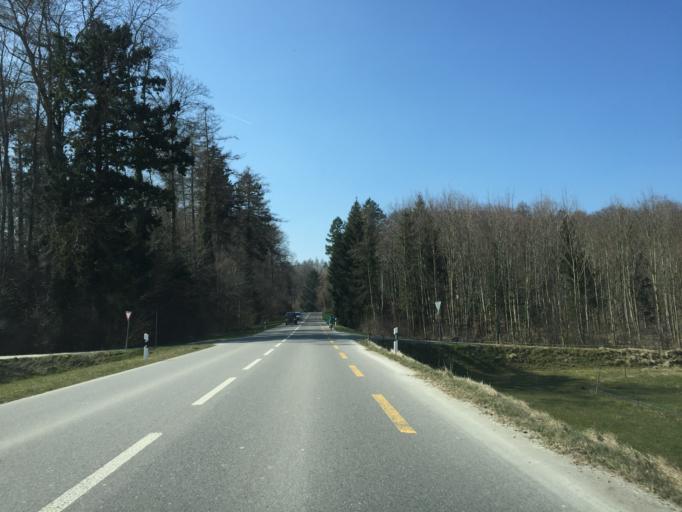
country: CH
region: Vaud
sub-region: Morges District
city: Cossonay
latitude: 46.6162
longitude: 6.4937
